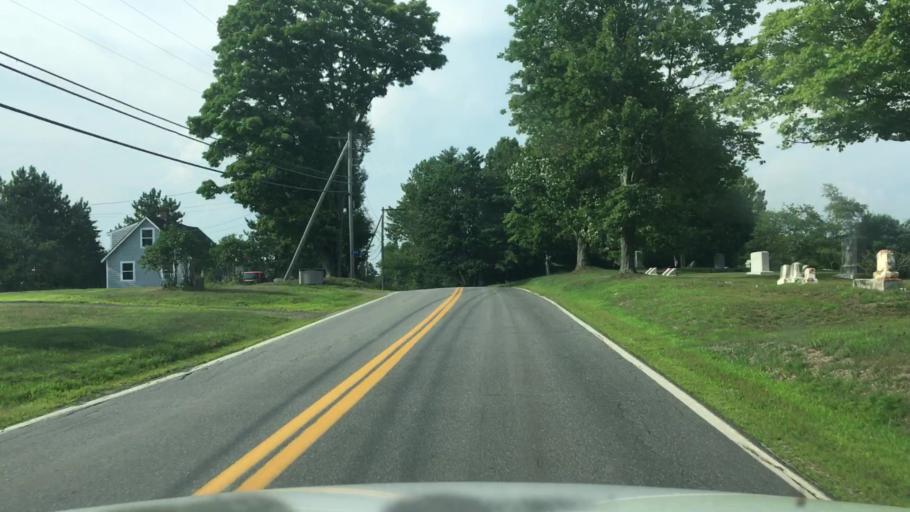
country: US
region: Maine
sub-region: Lincoln County
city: Waldoboro
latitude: 44.1186
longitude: -69.3642
